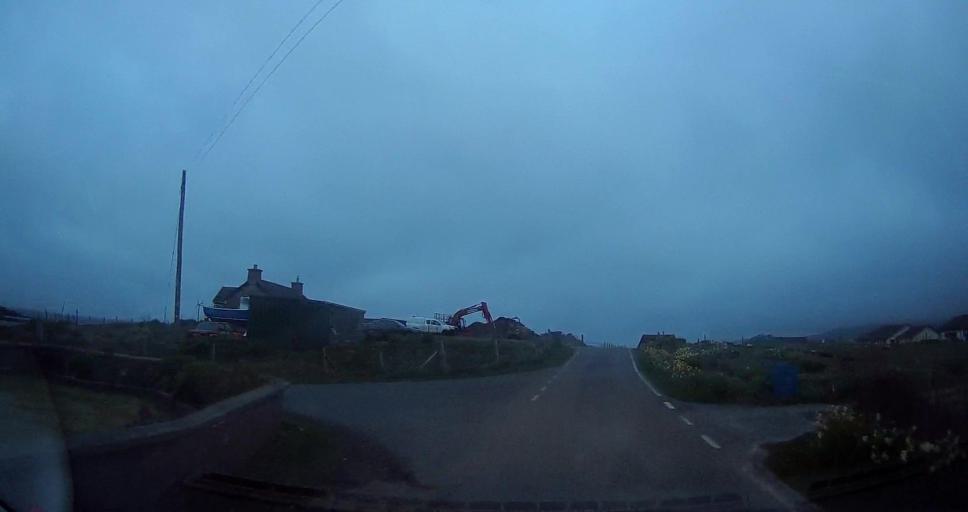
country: GB
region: Scotland
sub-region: Shetland Islands
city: Sandwick
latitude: 60.0385
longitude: -1.2179
